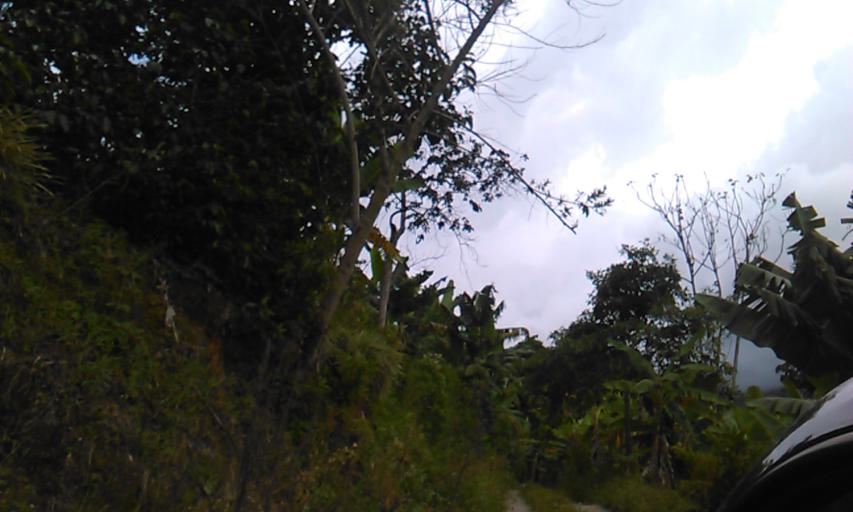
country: CO
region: Quindio
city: Cordoba
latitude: 4.4086
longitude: -75.6821
